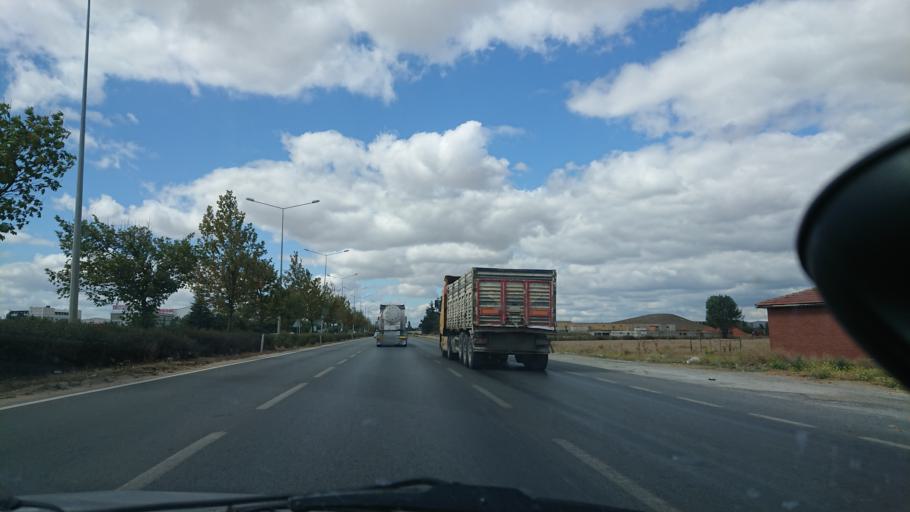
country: TR
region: Eskisehir
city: Eskisehir
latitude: 39.7989
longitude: 30.4418
